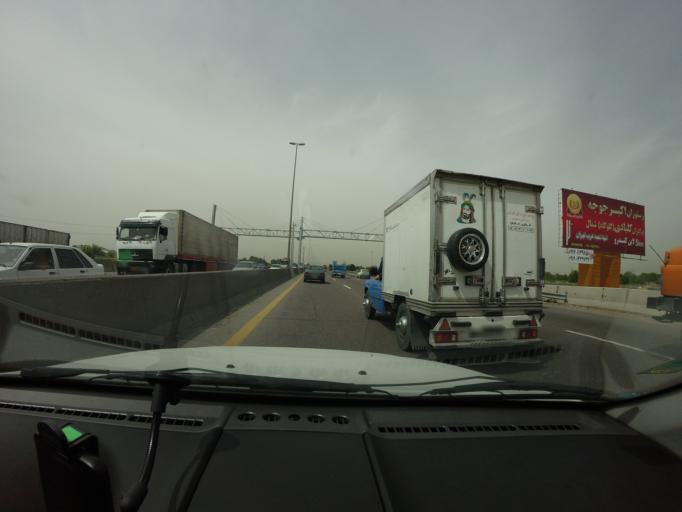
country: IR
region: Tehran
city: Eslamshahr
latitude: 35.5803
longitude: 51.1565
